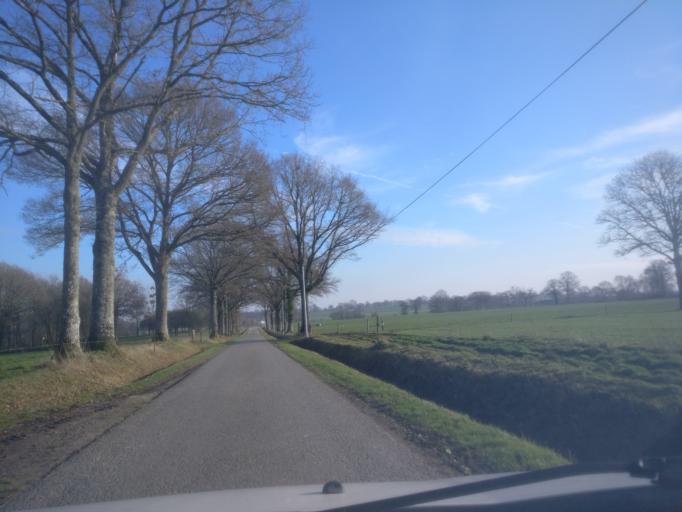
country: FR
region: Brittany
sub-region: Departement d'Ille-et-Vilaine
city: Livre-sur-Changeon
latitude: 48.2168
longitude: -1.3130
